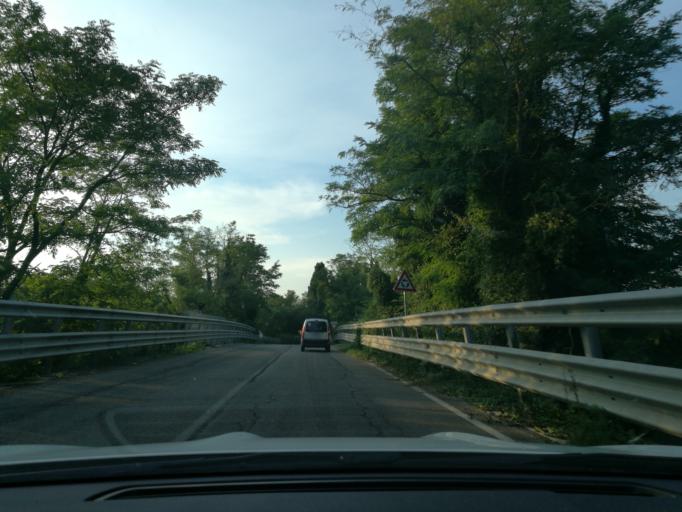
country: IT
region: Umbria
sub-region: Provincia di Terni
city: Acquasparta
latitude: 42.6806
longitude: 12.5502
